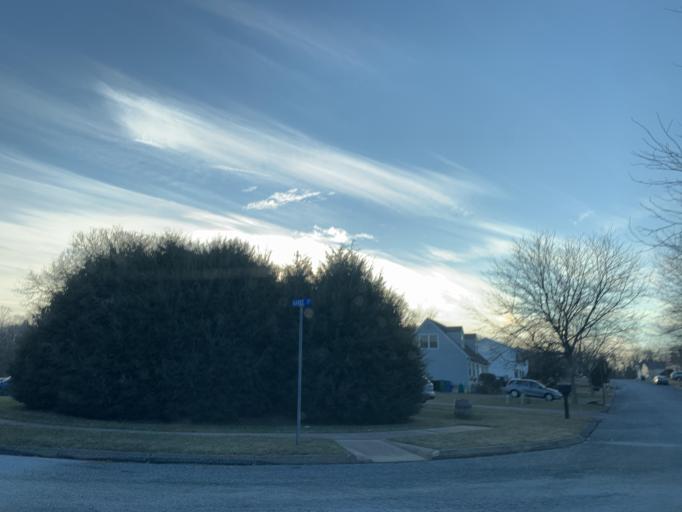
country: US
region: Rhode Island
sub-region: Washington County
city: Wakefield-Peacedale
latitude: 41.4500
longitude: -71.5081
